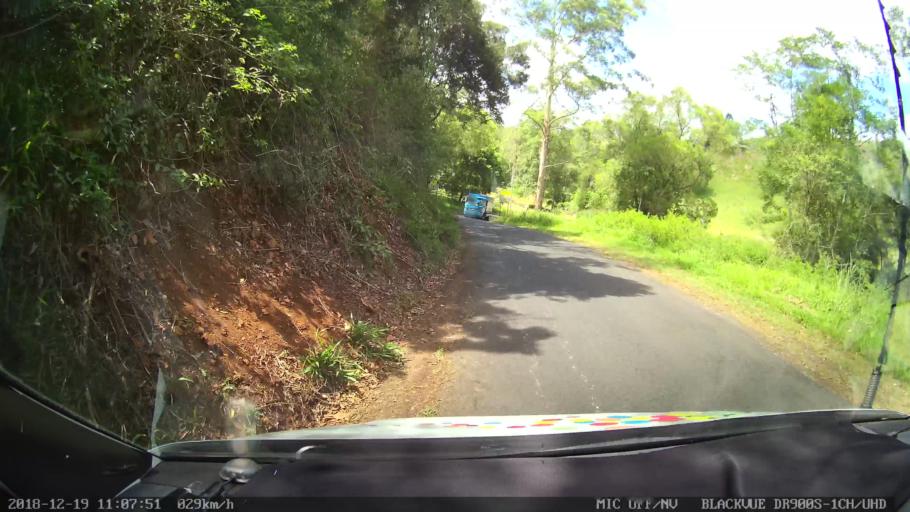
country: AU
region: New South Wales
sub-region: Lismore Municipality
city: Nimbin
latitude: -28.6283
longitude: 153.2670
